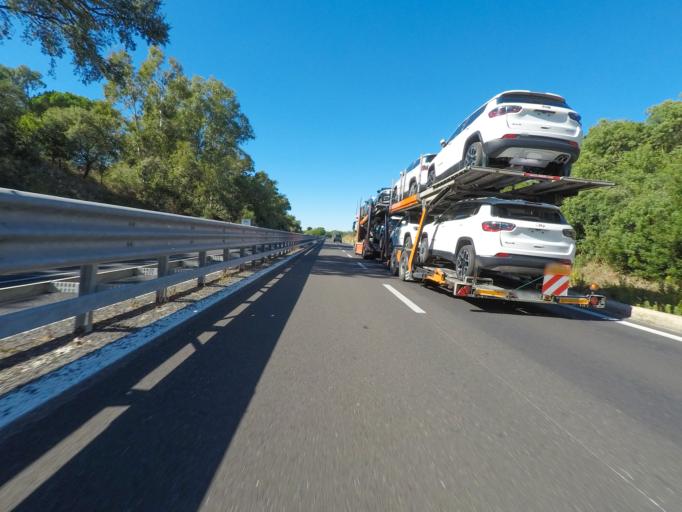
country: IT
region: Latium
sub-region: Provincia di Viterbo
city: Montalto di Castro
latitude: 42.3062
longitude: 11.6611
